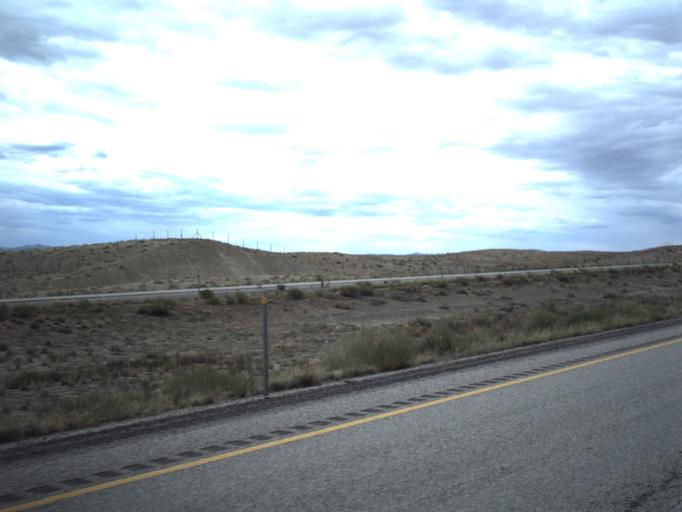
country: US
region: Utah
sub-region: Grand County
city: Moab
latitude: 39.0166
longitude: -109.3020
